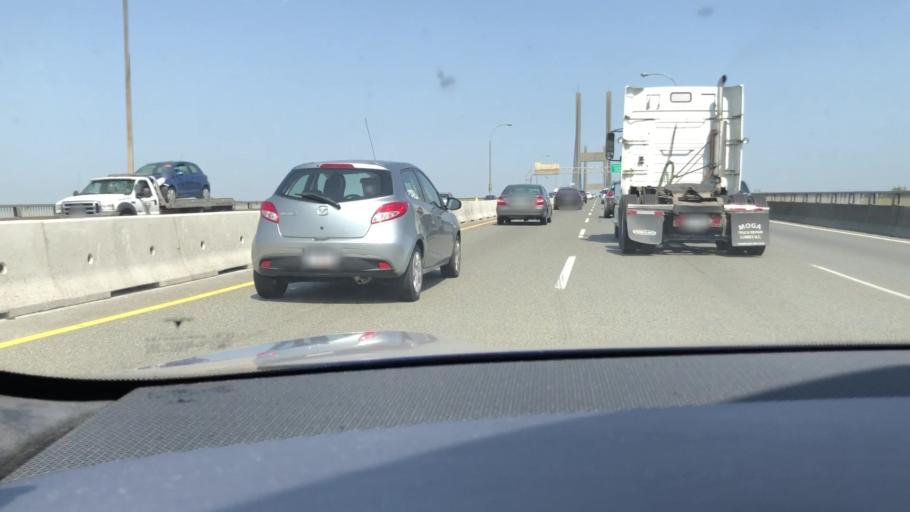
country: CA
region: British Columbia
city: Delta
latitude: 49.1505
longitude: -122.9391
